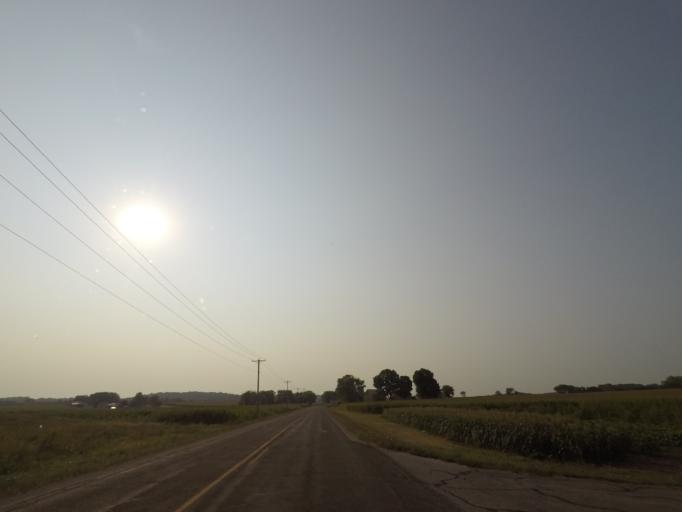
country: US
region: Wisconsin
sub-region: Dane County
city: Cottage Grove
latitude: 43.0507
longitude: -89.2441
